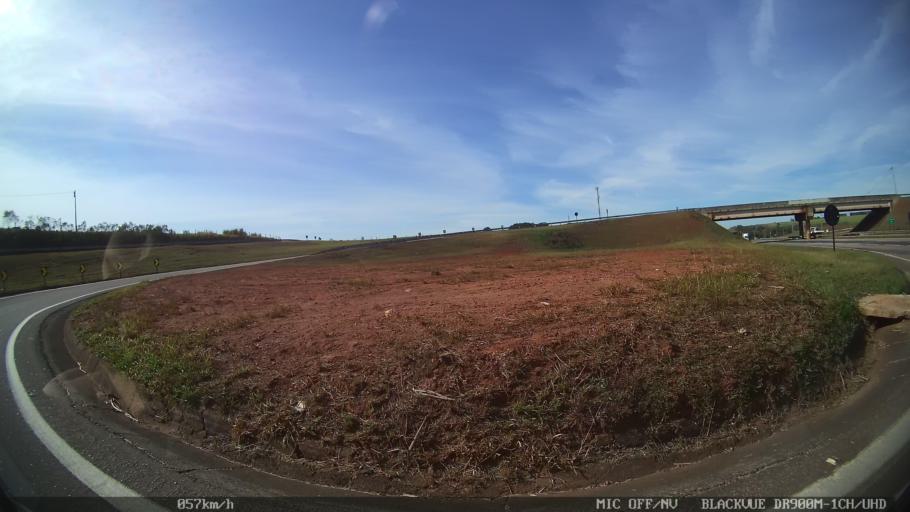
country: BR
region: Sao Paulo
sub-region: Rio Das Pedras
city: Rio das Pedras
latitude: -22.7820
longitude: -47.5875
